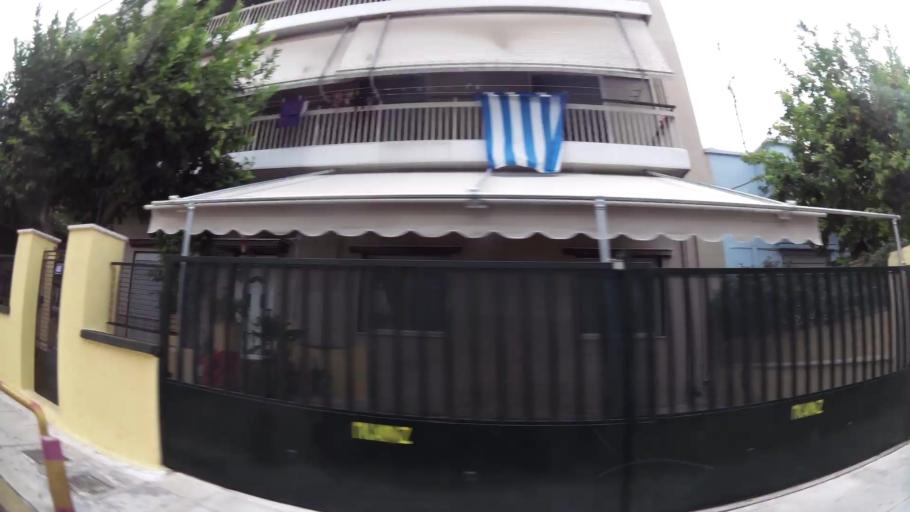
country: GR
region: Attica
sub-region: Nomos Piraios
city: Agios Ioannis Rentis
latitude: 37.9582
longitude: 23.6608
